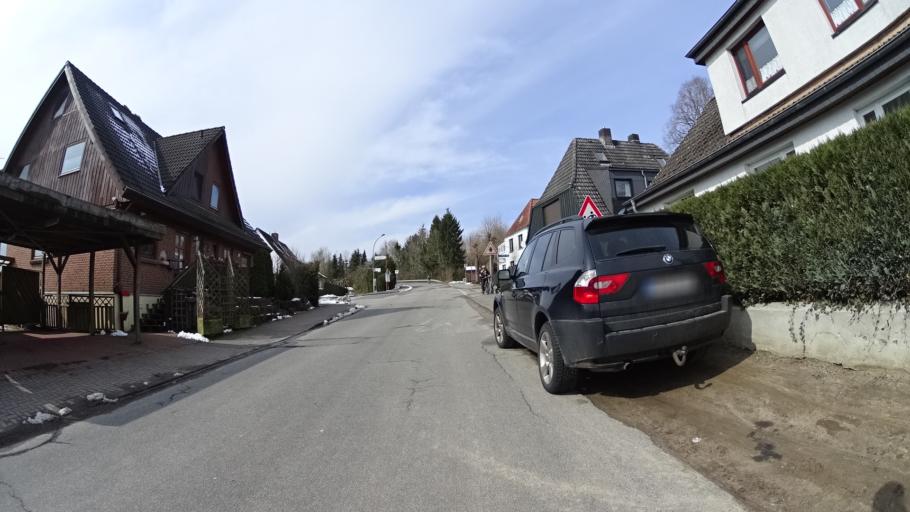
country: DE
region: Schleswig-Holstein
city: Stolpe
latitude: 54.1305
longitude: 10.2190
